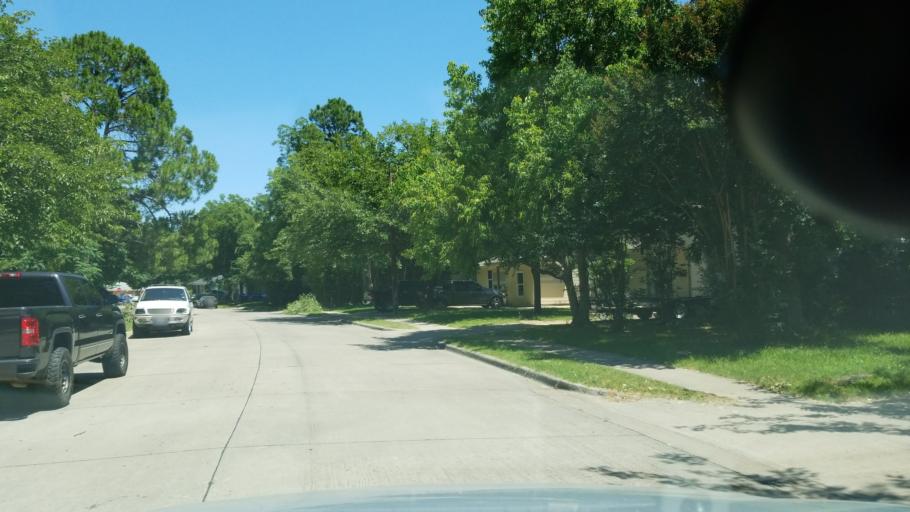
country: US
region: Texas
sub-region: Dallas County
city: Irving
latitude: 32.8316
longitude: -96.9320
